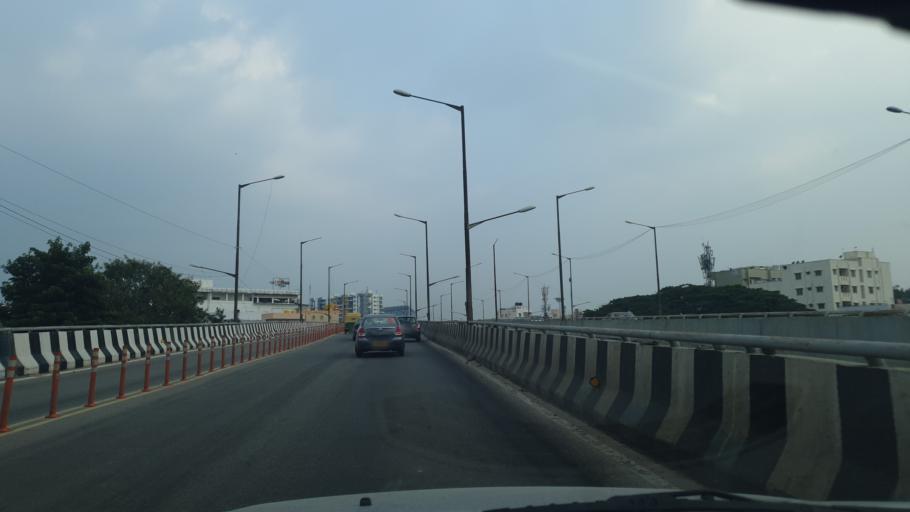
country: IN
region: Karnataka
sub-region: Bangalore Urban
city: Bangalore
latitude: 12.9924
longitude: 77.6868
